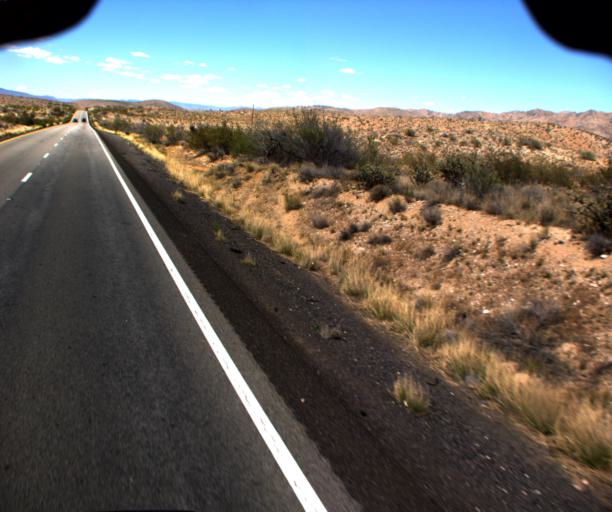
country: US
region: Arizona
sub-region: Mohave County
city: Kingman
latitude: 34.9784
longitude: -113.6683
